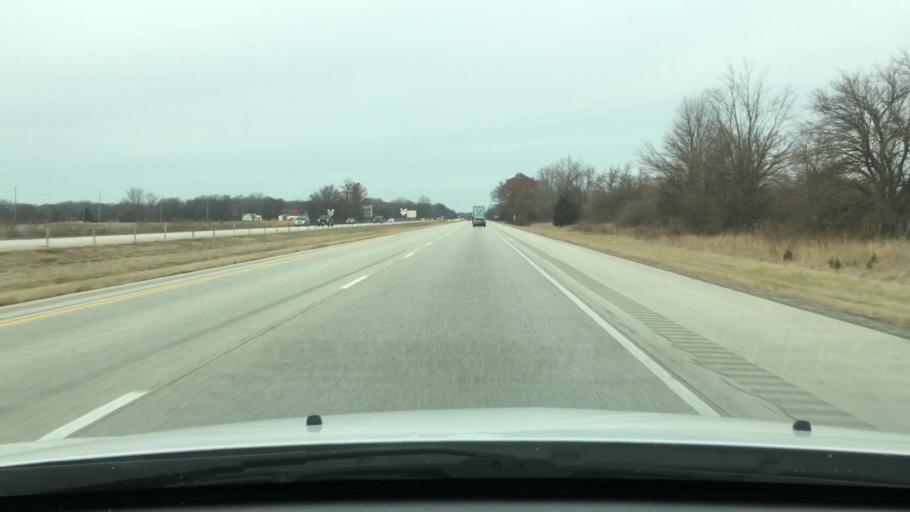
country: US
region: Illinois
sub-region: Sangamon County
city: Grandview
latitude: 39.8494
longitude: -89.5944
